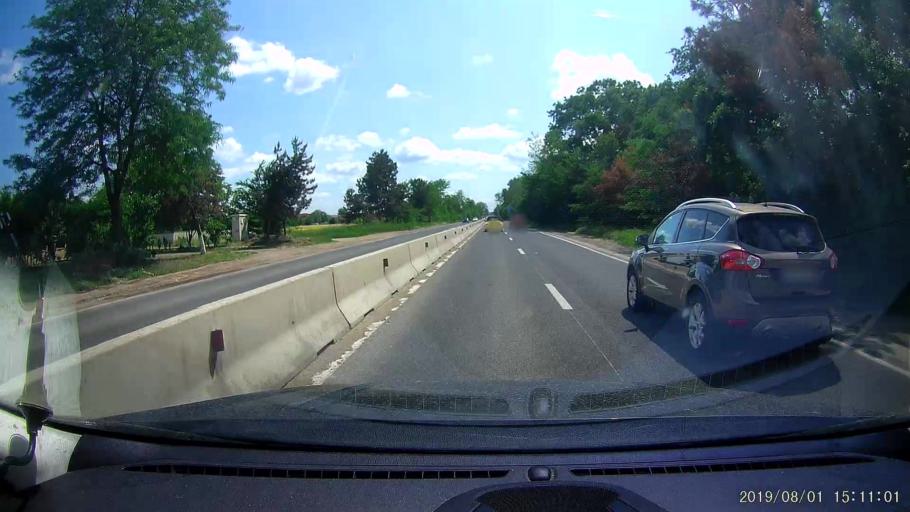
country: RO
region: Braila
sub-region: Comuna Chiscani
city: Chiscani
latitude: 45.2219
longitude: 27.9279
